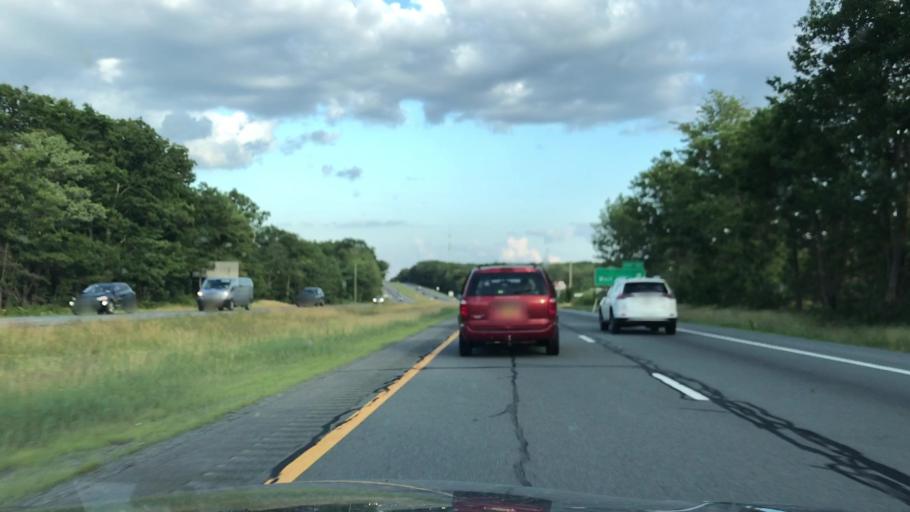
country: US
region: New York
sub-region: Sullivan County
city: Rock Hill
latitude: 41.6079
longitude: -74.5670
